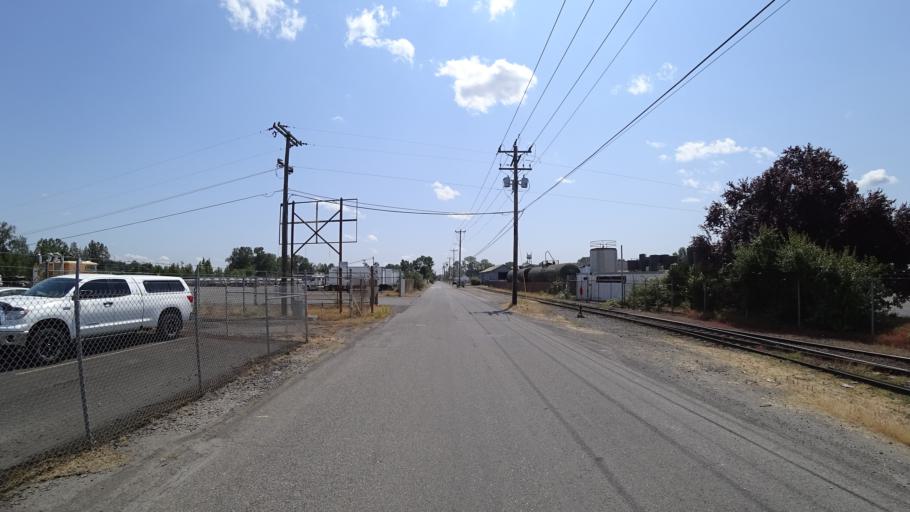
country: US
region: Washington
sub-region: Clark County
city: Vancouver
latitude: 45.6150
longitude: -122.7119
